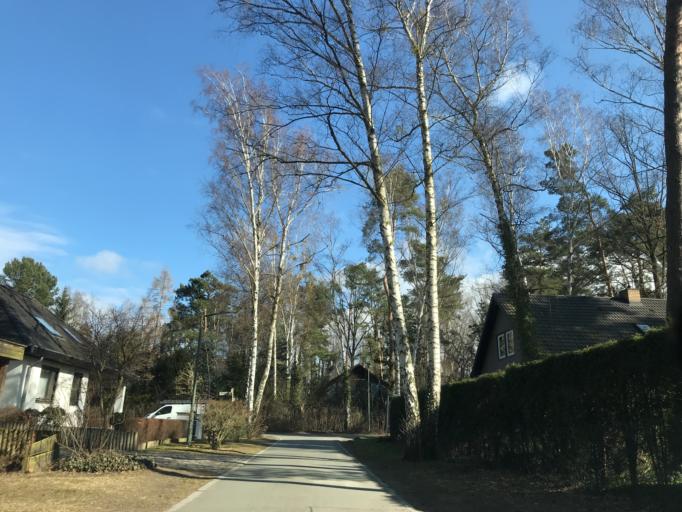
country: DE
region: Berlin
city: Kladow
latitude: 52.4565
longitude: 13.1218
